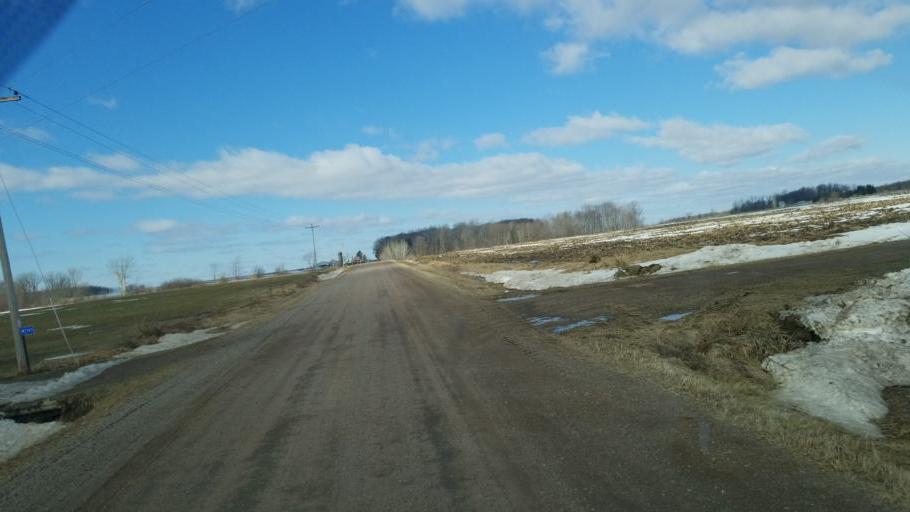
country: US
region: Wisconsin
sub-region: Clark County
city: Loyal
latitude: 44.6834
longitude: -90.4477
